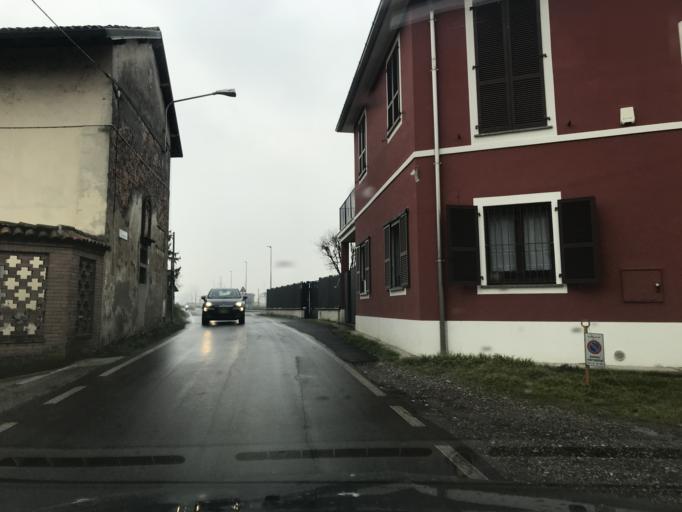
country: IT
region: Lombardy
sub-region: Provincia di Lodi
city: Villanova del Sillaro
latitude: 45.2383
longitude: 9.4799
